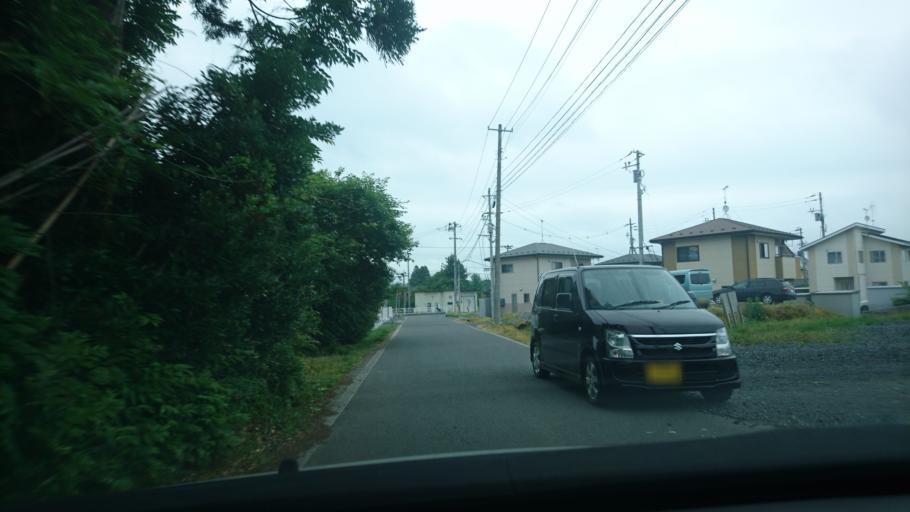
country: JP
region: Iwate
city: Ichinoseki
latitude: 38.9175
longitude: 141.0921
